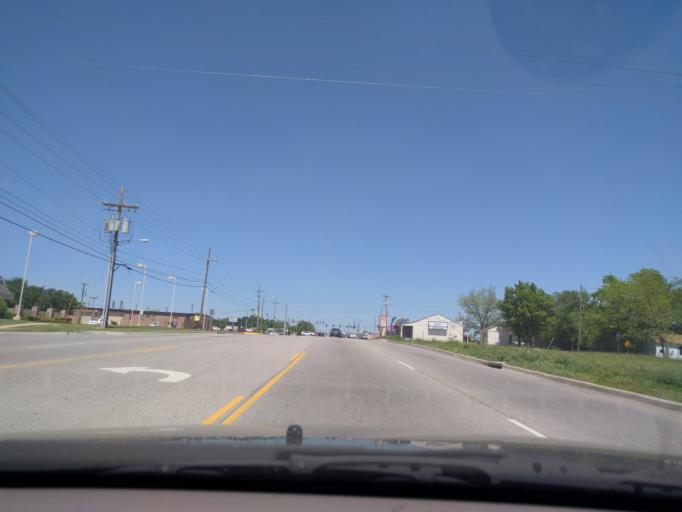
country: US
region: Oklahoma
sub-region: Tulsa County
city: Broken Arrow
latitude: 36.0587
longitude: -95.7974
